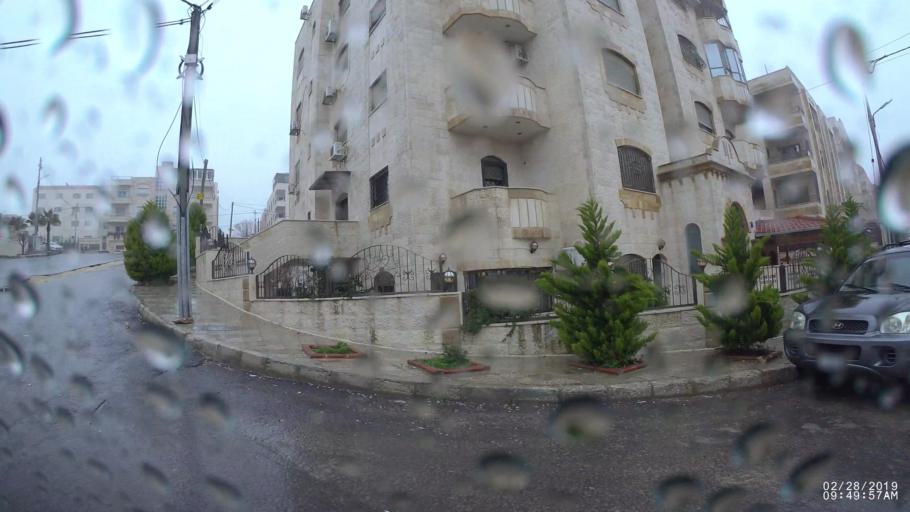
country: JO
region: Amman
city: Al Jubayhah
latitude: 32.0188
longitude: 35.8859
